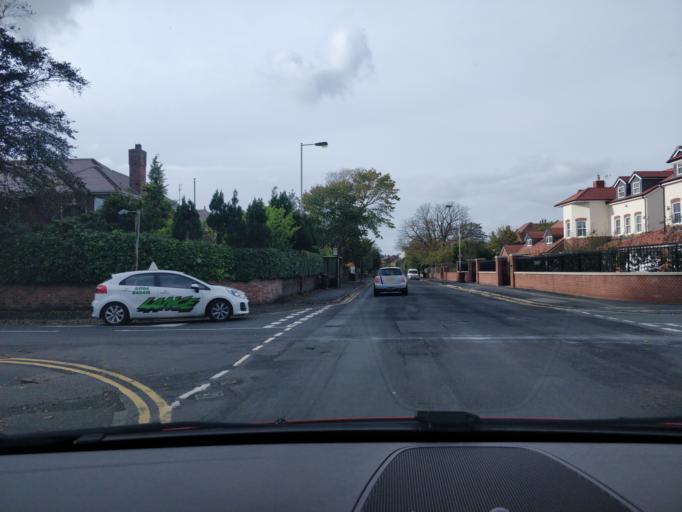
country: GB
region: England
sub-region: Sefton
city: Southport
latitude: 53.6303
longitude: -3.0211
